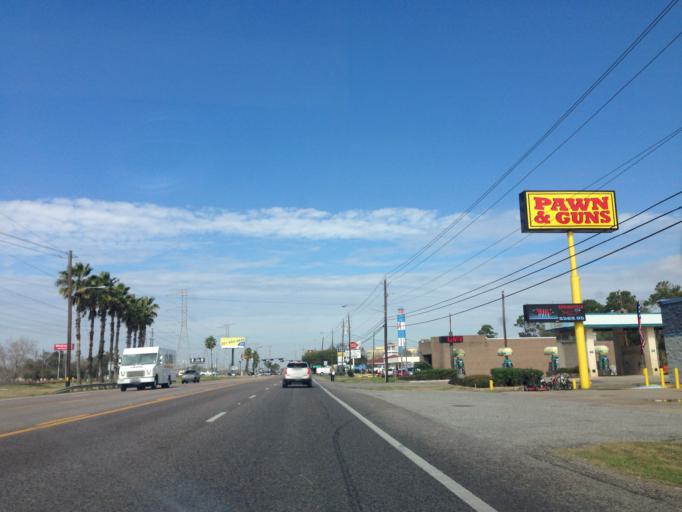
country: US
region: Texas
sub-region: Galveston County
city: Kemah
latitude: 29.5359
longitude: -95.0168
